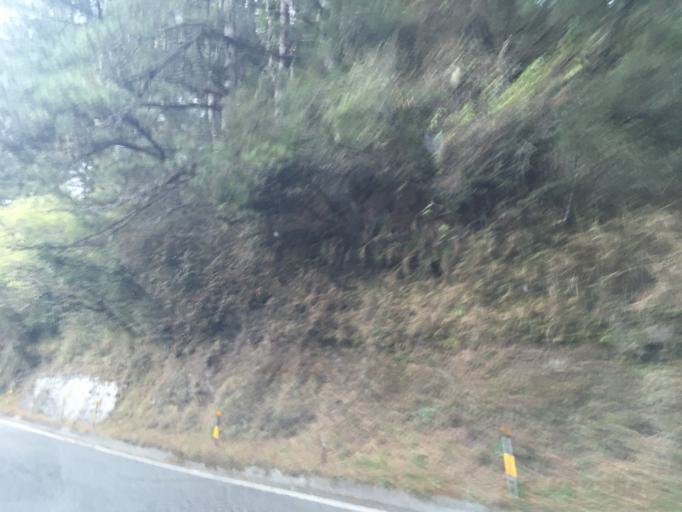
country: TW
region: Taiwan
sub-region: Hualien
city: Hualian
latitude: 24.1789
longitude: 121.3015
